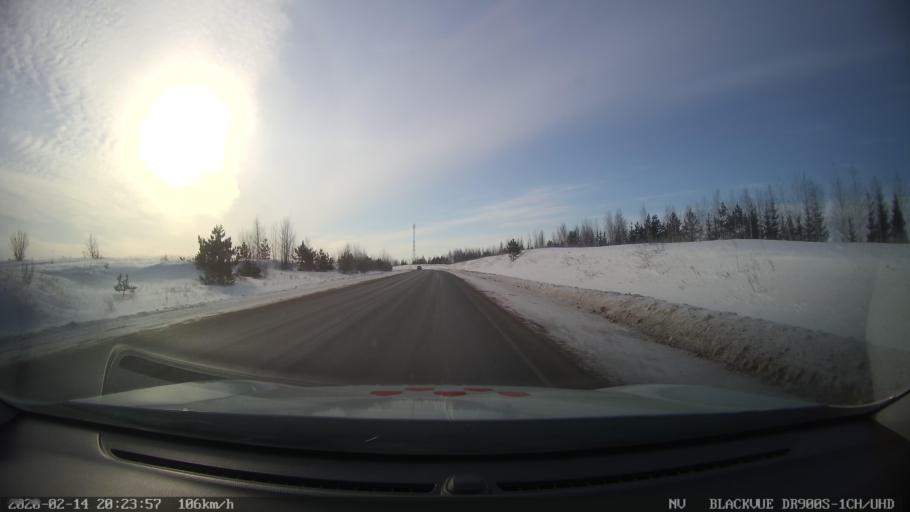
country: RU
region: Tatarstan
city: Verkhniy Uslon
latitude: 55.5201
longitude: 48.9676
